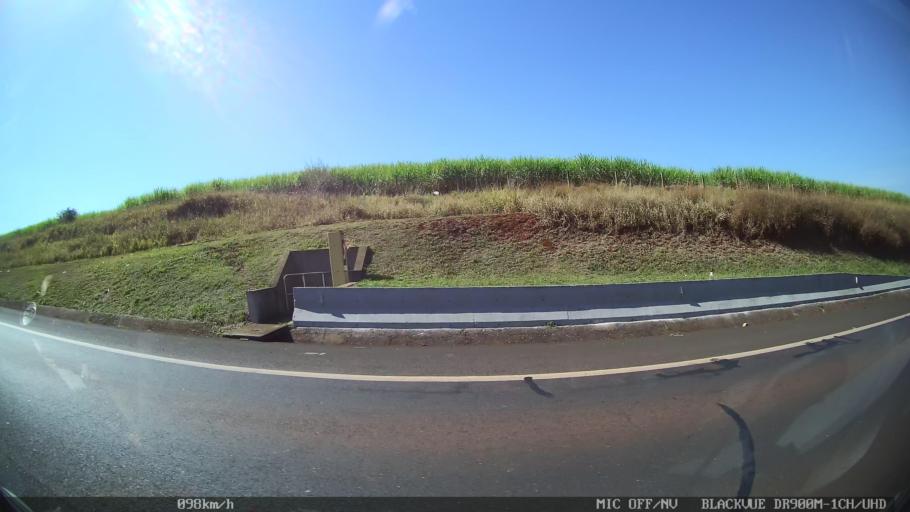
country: BR
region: Sao Paulo
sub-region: Batatais
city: Batatais
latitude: -20.8390
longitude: -47.6015
